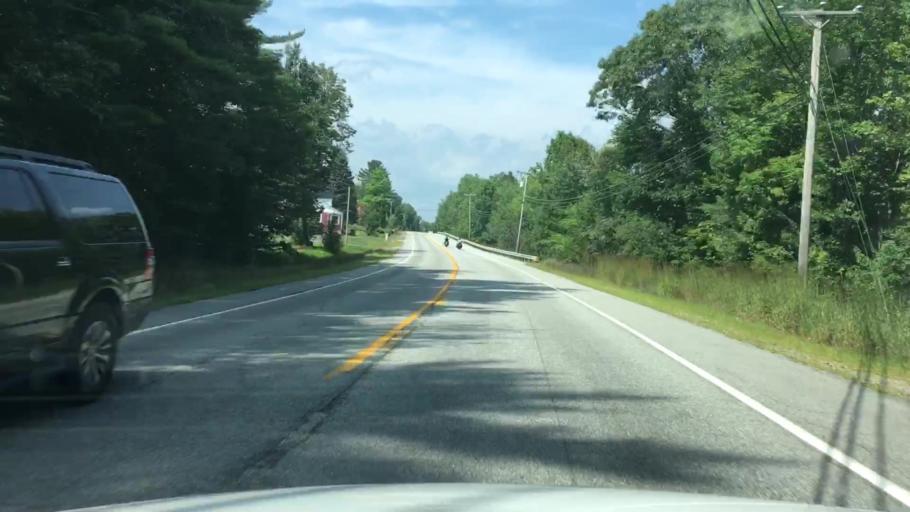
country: US
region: Maine
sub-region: Oxford County
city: Peru
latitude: 44.4948
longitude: -70.3879
